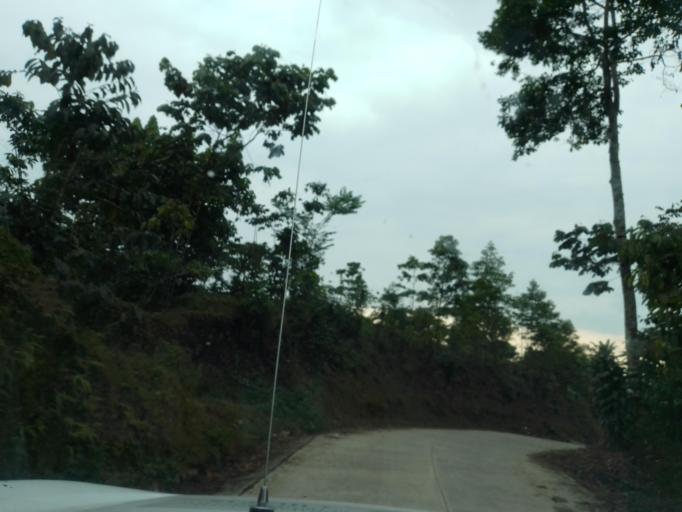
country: MX
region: Chiapas
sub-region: Union Juarez
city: Santo Domingo
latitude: 15.0601
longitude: -92.1096
